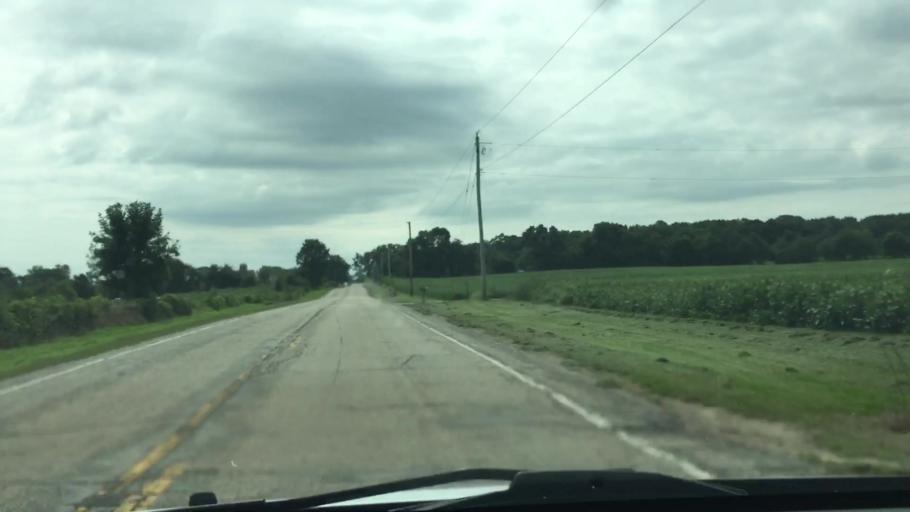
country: US
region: Wisconsin
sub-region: Dane County
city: Belleville
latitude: 42.8914
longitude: -89.4822
